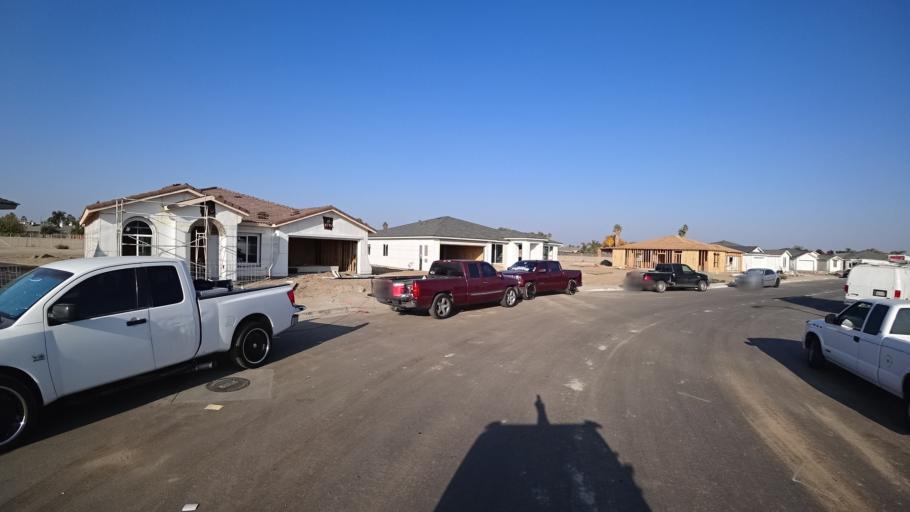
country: US
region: California
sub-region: Kern County
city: Greenfield
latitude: 35.2917
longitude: -119.0178
